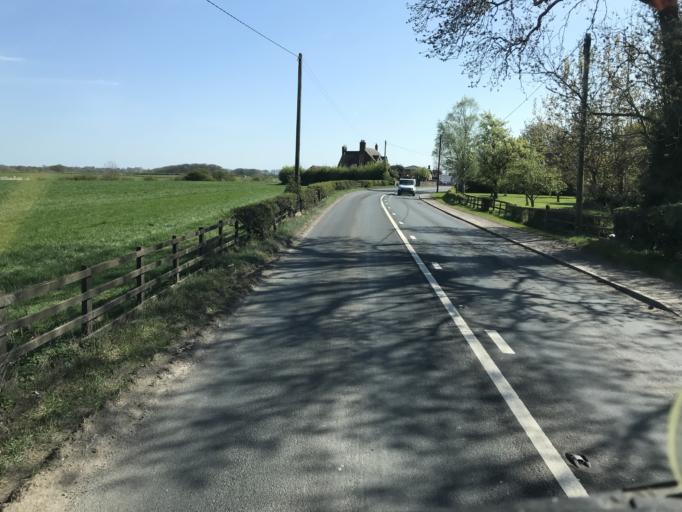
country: GB
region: England
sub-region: Cheshire East
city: Middlewich
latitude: 53.1990
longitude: -2.4091
